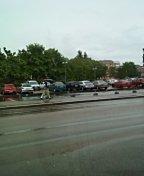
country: SE
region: Vaestmanland
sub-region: Kopings Kommun
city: Koping
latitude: 59.5177
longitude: 15.9931
